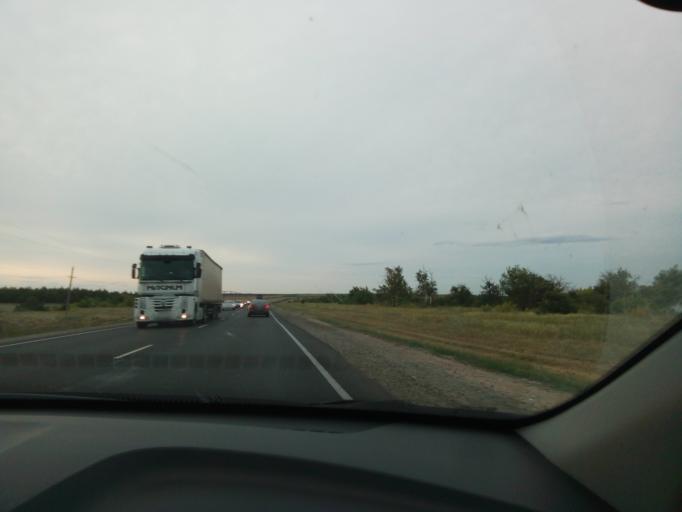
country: RU
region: Volgograd
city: Dubovka
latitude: 49.1147
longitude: 44.8118
